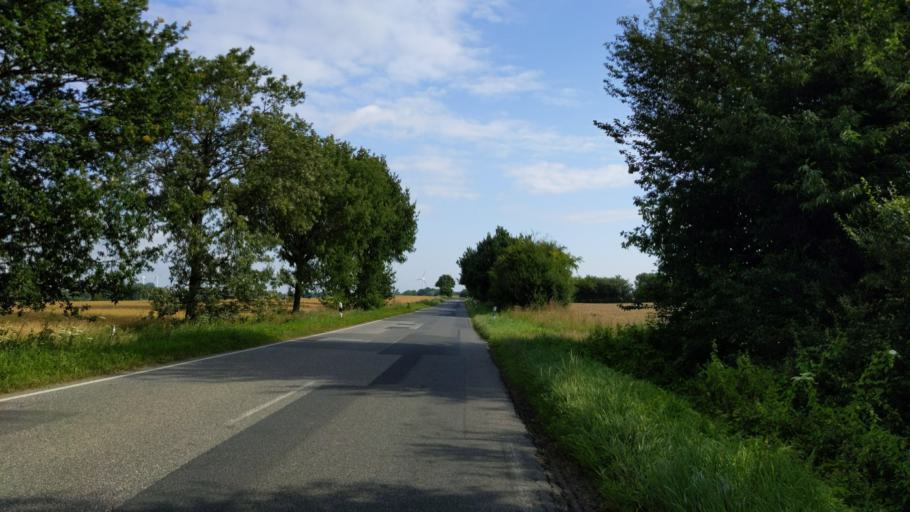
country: DE
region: Schleswig-Holstein
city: Bad Schwartau
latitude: 53.9787
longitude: 10.6573
